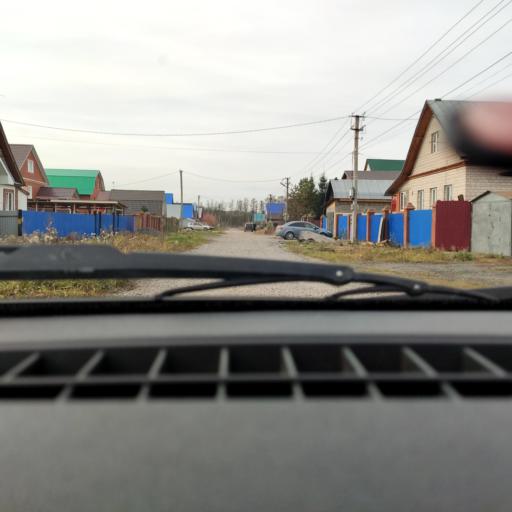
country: RU
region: Bashkortostan
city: Iglino
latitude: 54.8138
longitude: 56.1867
